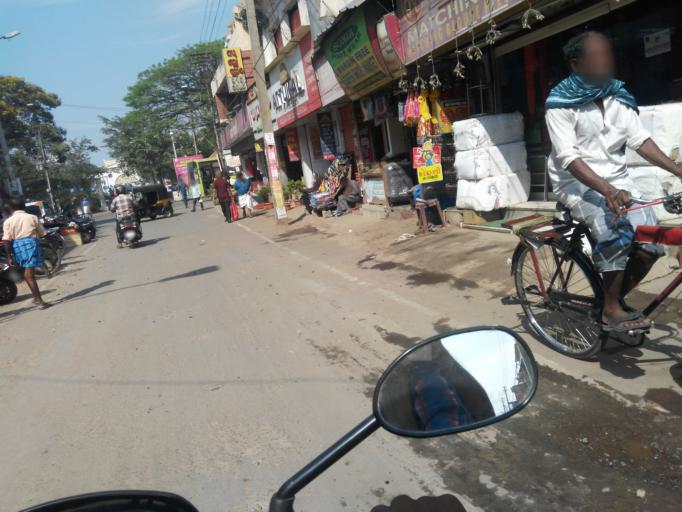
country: IN
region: Kerala
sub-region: Thiruvananthapuram
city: Thiruvananthapuram
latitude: 8.4828
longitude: 76.9488
